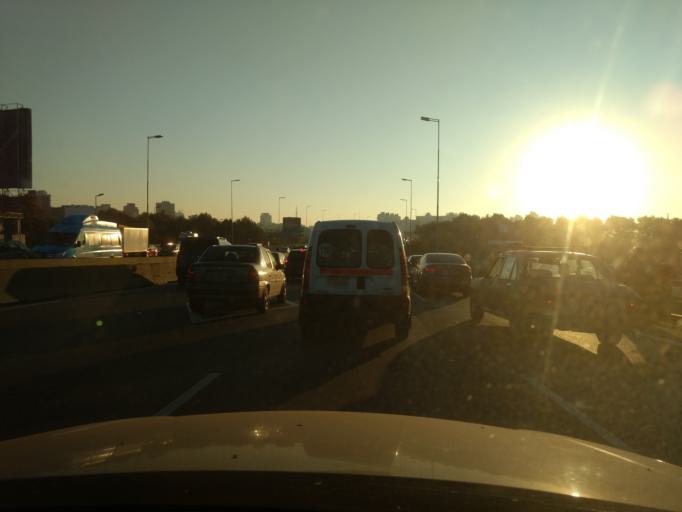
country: AR
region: Buenos Aires F.D.
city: Villa Santa Rita
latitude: -34.6394
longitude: -58.4572
